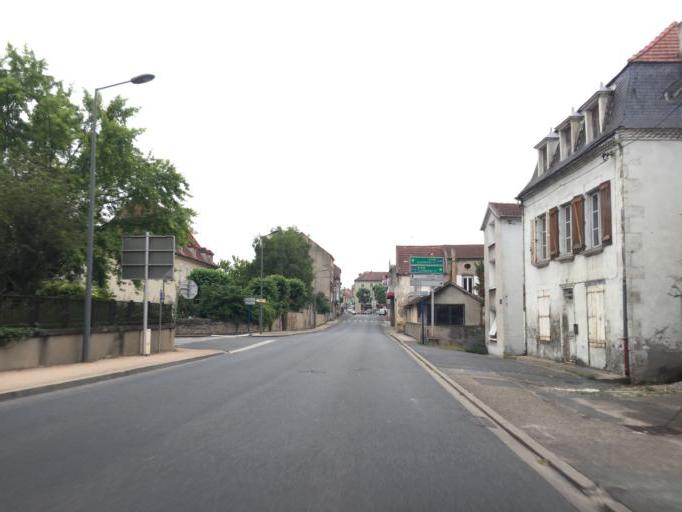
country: FR
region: Auvergne
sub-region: Departement de l'Allier
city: Gannat
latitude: 46.1037
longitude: 3.1963
